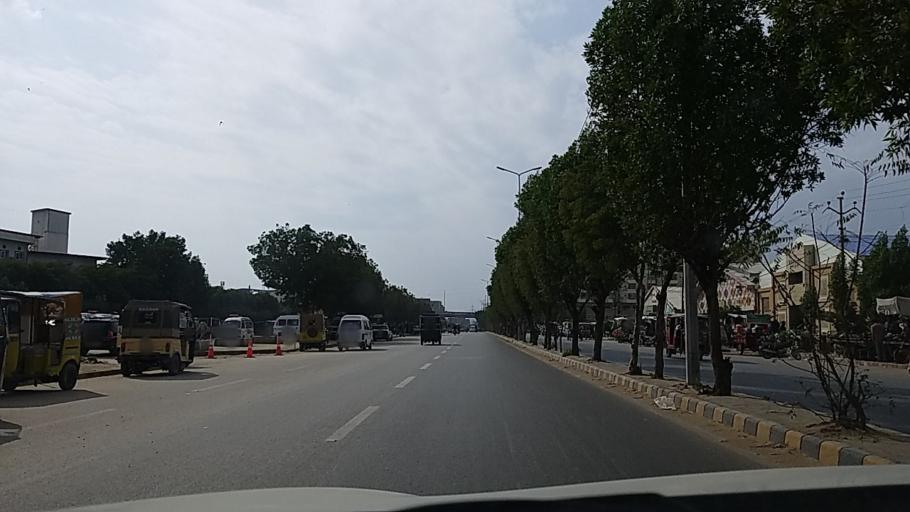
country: PK
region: Sindh
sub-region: Karachi District
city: Karachi
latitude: 24.8177
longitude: 67.1112
